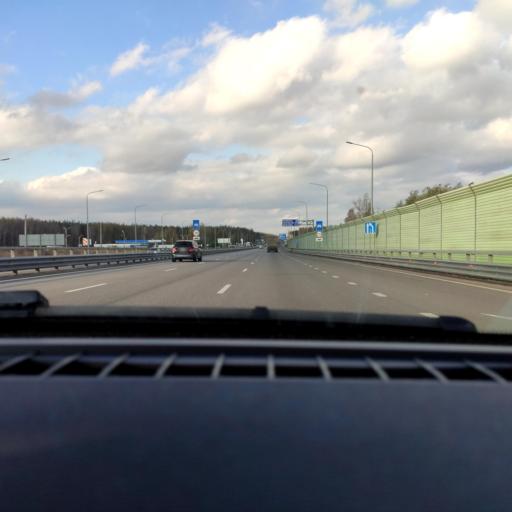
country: RU
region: Voronezj
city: Somovo
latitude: 51.6811
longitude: 39.3021
